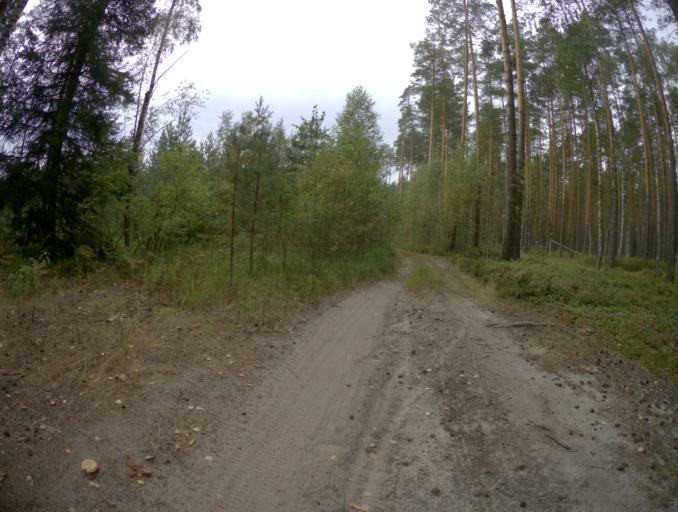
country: RU
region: Vladimir
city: Ivanishchi
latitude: 55.8439
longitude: 40.3378
